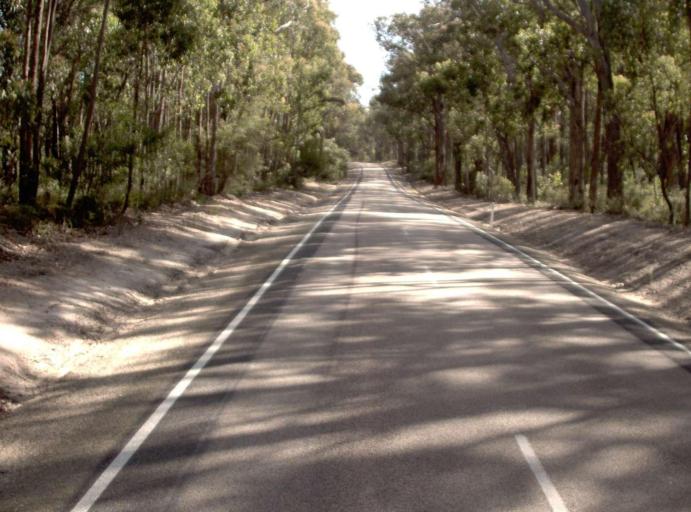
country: AU
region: Victoria
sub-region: East Gippsland
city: Lakes Entrance
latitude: -37.6849
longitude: 148.0506
